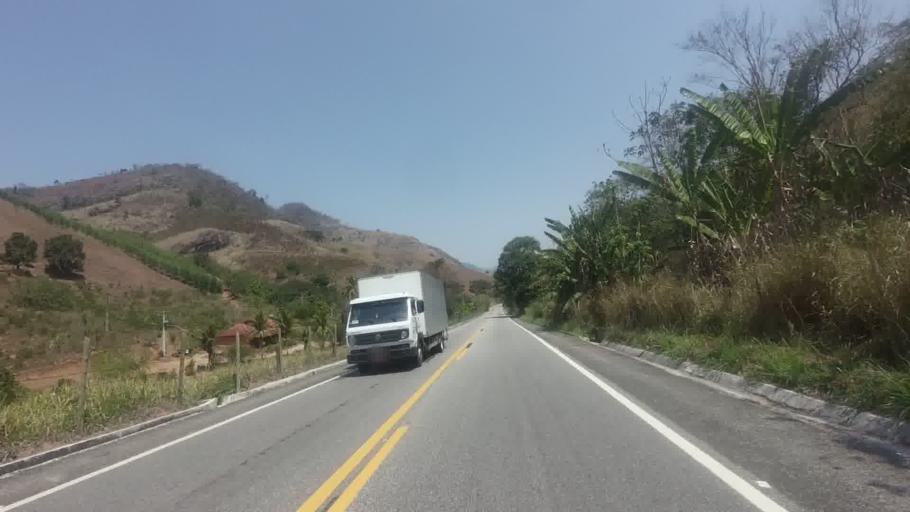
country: BR
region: Espirito Santo
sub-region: Cachoeiro De Itapemirim
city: Cachoeiro de Itapemirim
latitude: -20.8497
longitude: -41.2433
